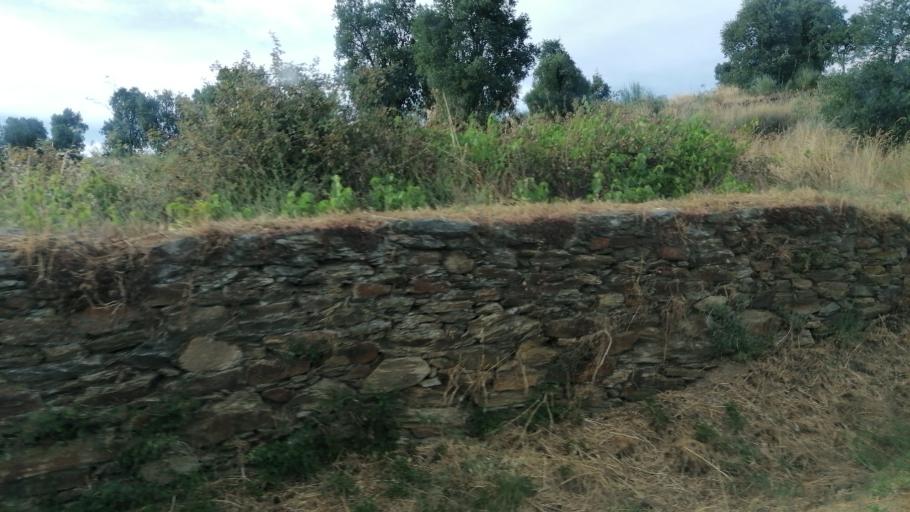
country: PT
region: Guarda
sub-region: Vila Nova de Foz Coa
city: Custoias
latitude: 41.0686
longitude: -7.3908
